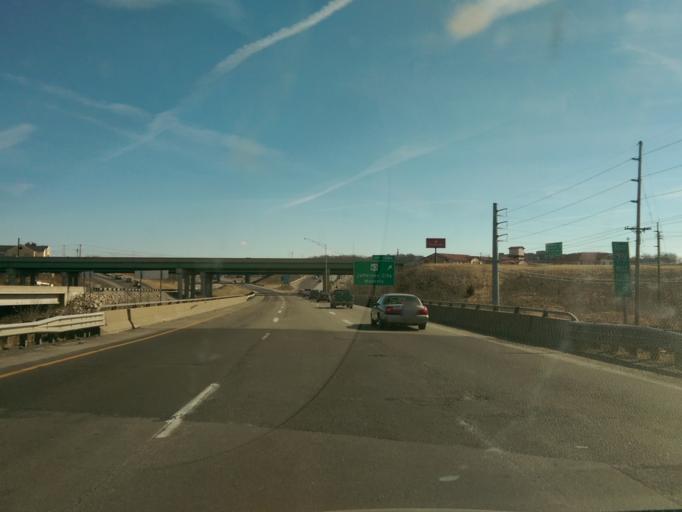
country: US
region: Missouri
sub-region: Boone County
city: Columbia
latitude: 38.9624
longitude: -92.2970
